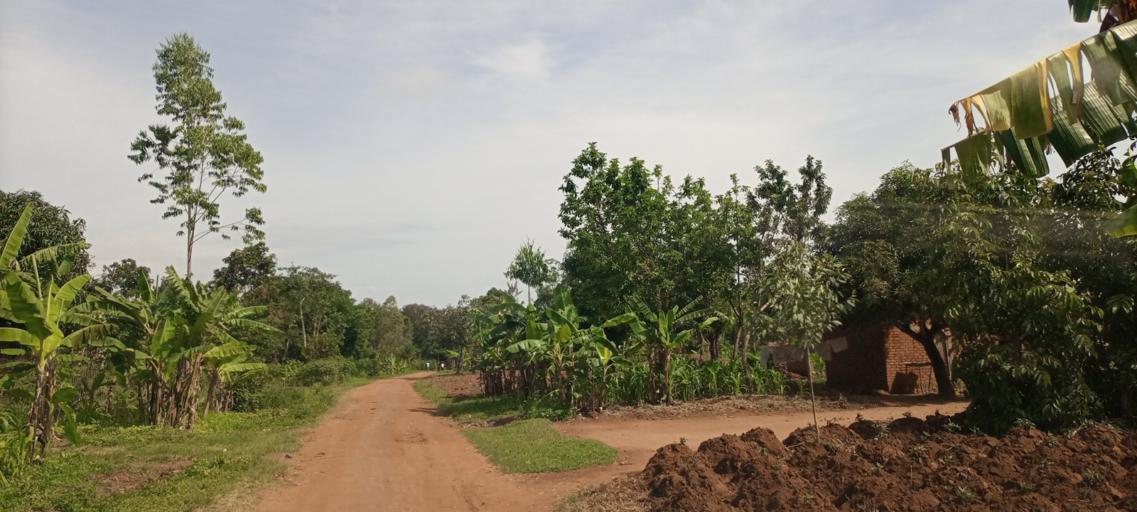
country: UG
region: Eastern Region
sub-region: Mbale District
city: Mbale
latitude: 1.1268
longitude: 34.0280
